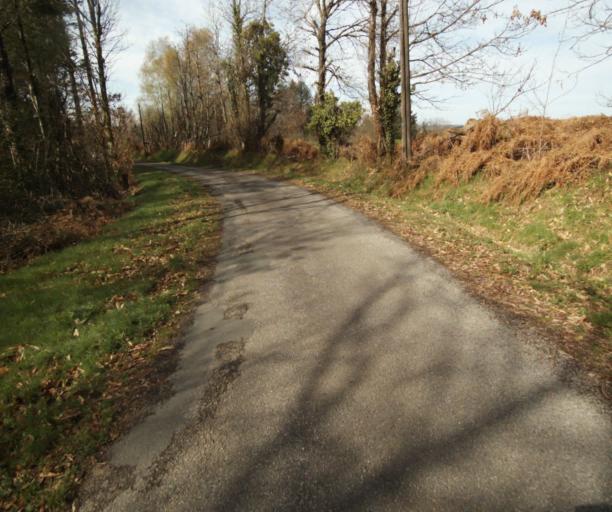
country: FR
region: Limousin
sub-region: Departement de la Correze
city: Tulle
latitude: 45.2846
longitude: 1.8226
